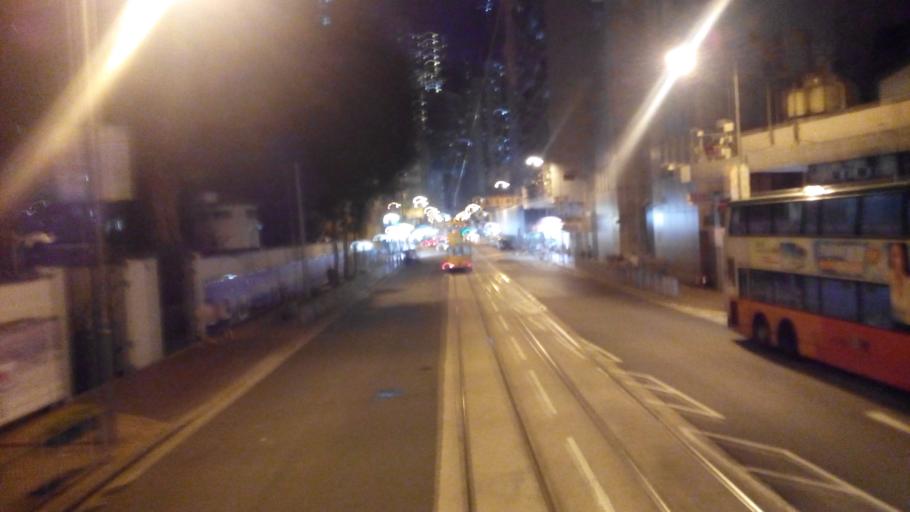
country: HK
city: Hong Kong
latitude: 22.2880
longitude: 114.1403
